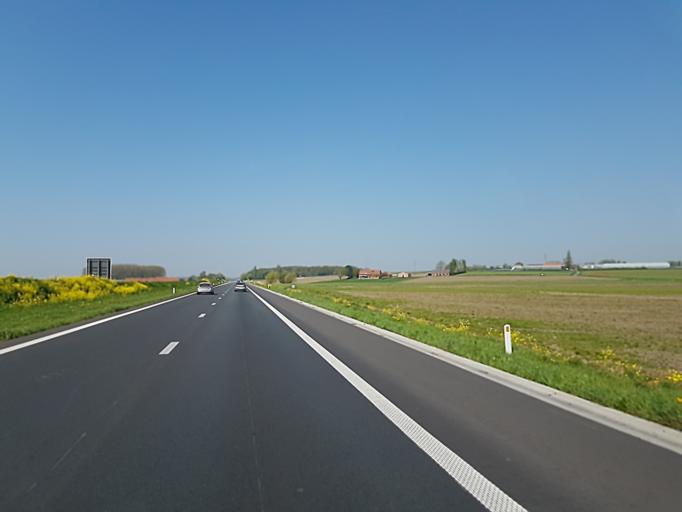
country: BE
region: Flanders
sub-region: Provincie West-Vlaanderen
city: Wervik
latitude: 50.8229
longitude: 3.0671
